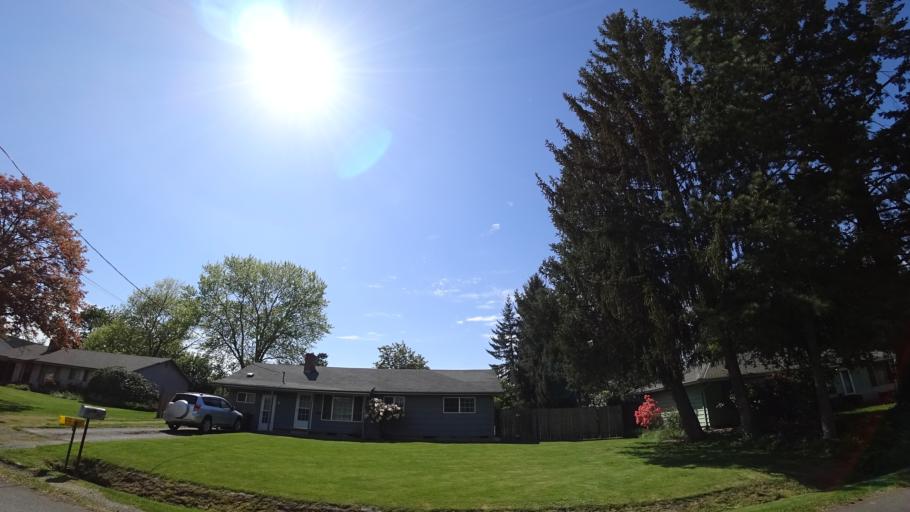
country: US
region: Oregon
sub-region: Washington County
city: Aloha
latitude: 45.4989
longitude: -122.8994
